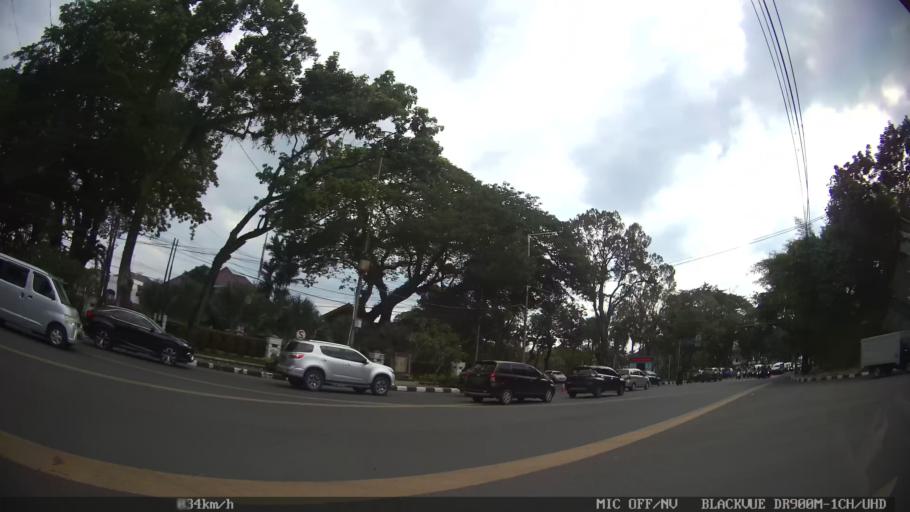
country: ID
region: North Sumatra
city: Medan
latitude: 3.5752
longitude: 98.6722
